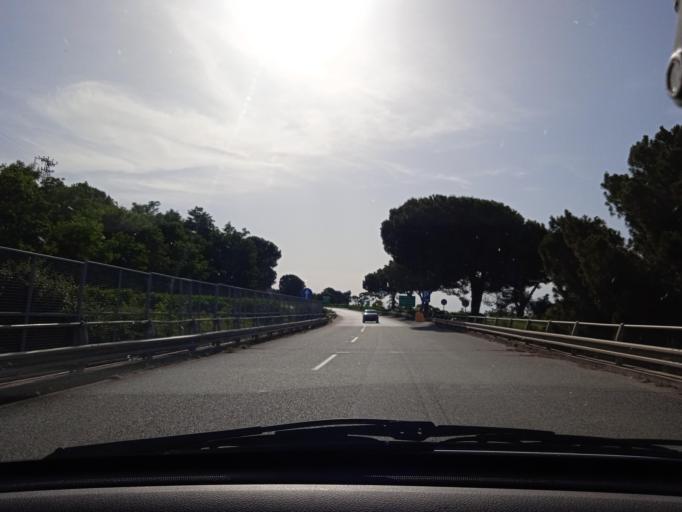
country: IT
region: Sicily
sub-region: Messina
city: Naso
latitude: 38.1506
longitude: 14.7724
